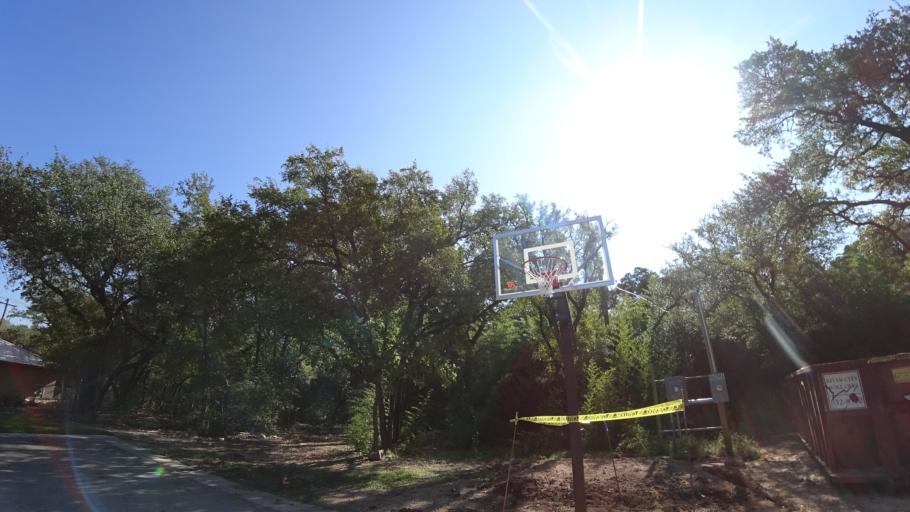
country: US
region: Texas
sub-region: Travis County
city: Rollingwood
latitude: 30.2647
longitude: -97.8100
